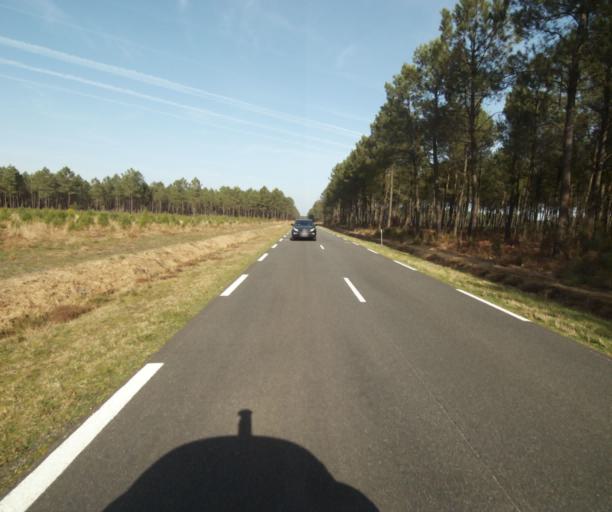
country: FR
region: Aquitaine
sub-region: Departement du Lot-et-Garonne
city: Casteljaloux
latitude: 44.1632
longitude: 0.0682
